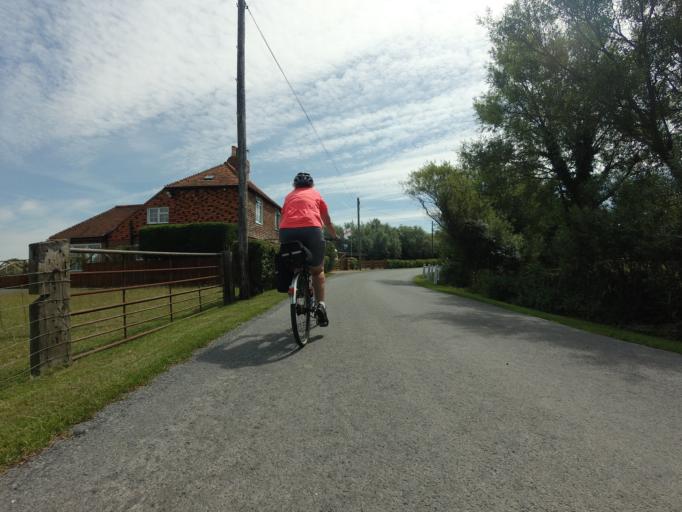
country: GB
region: England
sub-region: Kent
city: Stone
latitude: 50.9977
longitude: 0.8038
